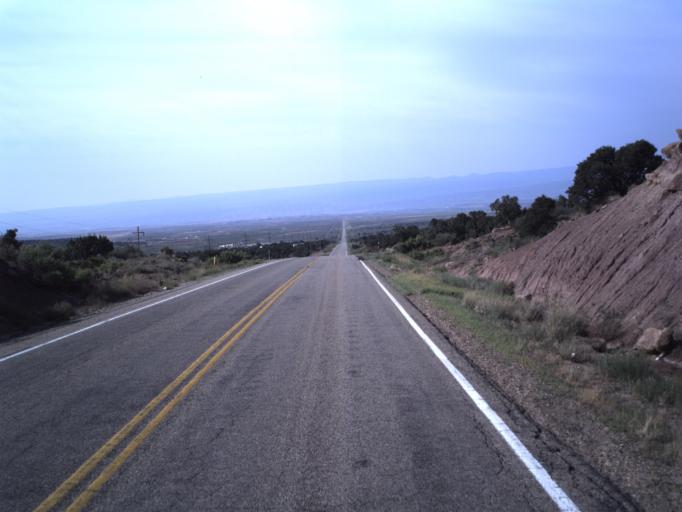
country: US
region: Utah
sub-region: Duchesne County
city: Duchesne
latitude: 40.3017
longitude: -110.3729
